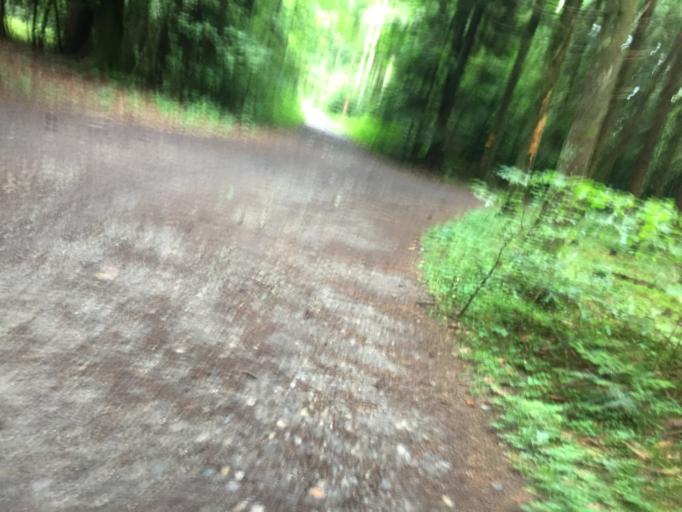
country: CH
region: Bern
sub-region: Bern-Mittelland District
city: Stettlen
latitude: 46.9262
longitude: 7.5214
